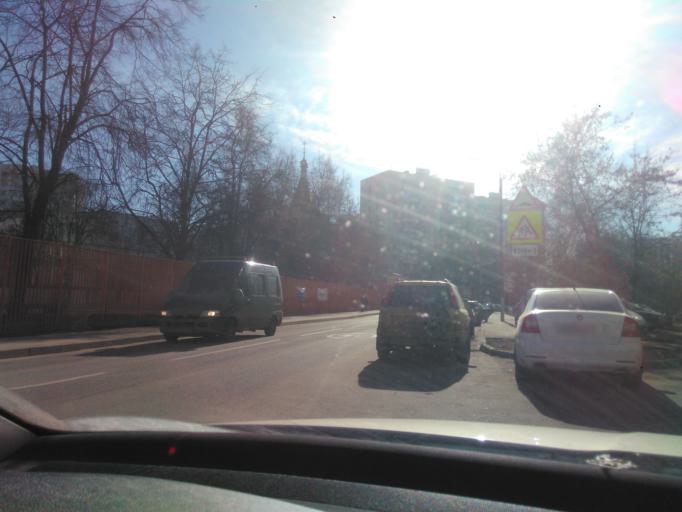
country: RU
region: Moscow
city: Zapadnoye Degunino
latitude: 55.8670
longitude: 37.5323
